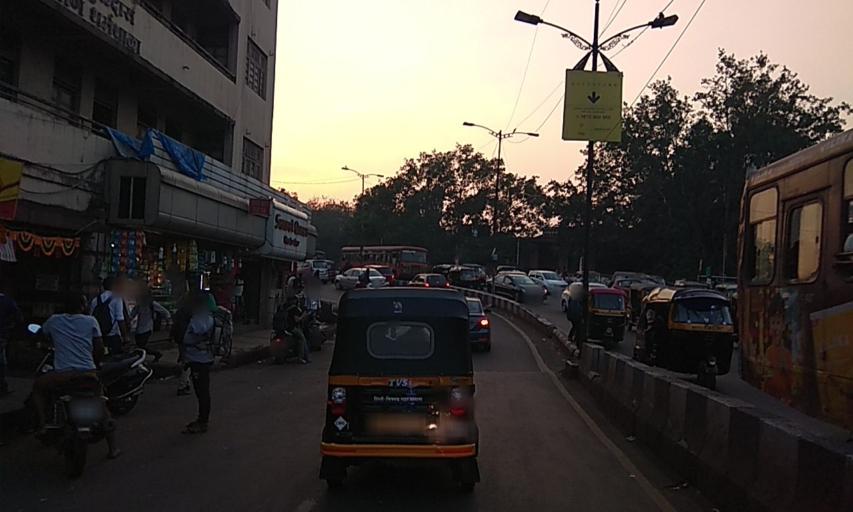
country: IN
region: Maharashtra
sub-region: Pune Division
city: Pune
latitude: 18.5283
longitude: 73.8740
